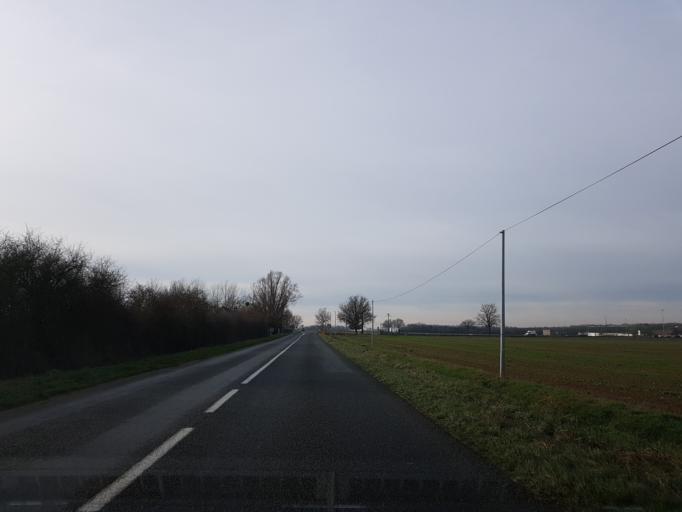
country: FR
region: Auvergne
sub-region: Departement de l'Allier
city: Yzeure
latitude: 46.5779
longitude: 3.4123
